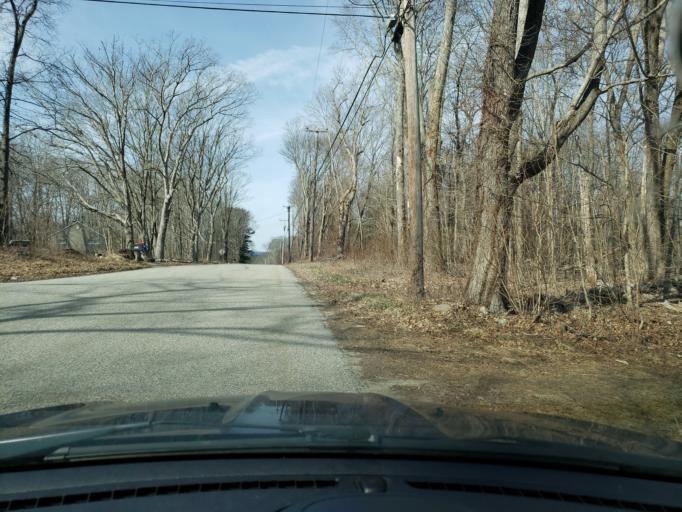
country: US
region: Connecticut
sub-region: Windham County
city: Danielson
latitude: 41.7888
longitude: -71.8531
